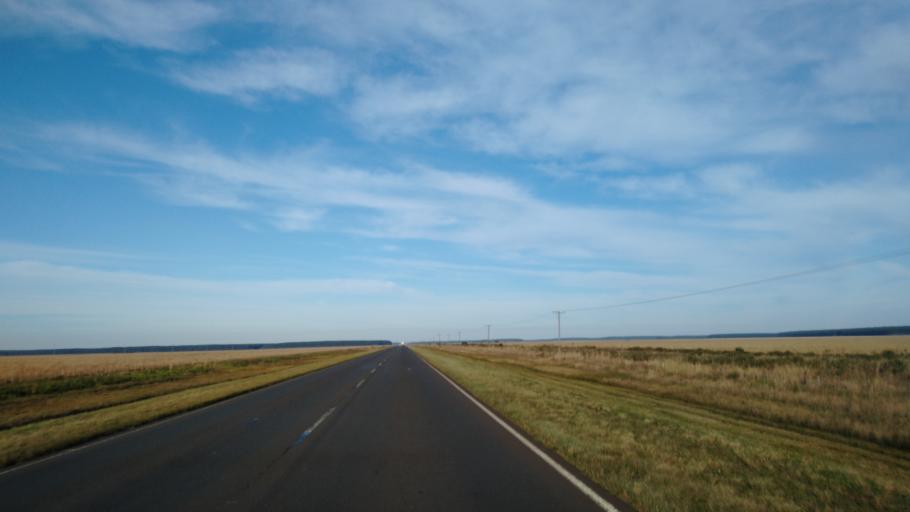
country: AR
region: Corrientes
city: La Cruz
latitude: -29.2804
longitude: -56.7609
